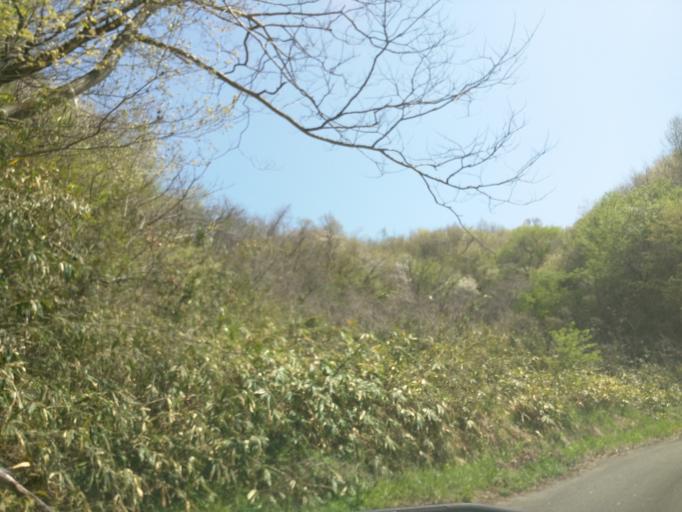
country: JP
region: Fukushima
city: Nihommatsu
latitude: 37.5661
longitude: 140.5192
